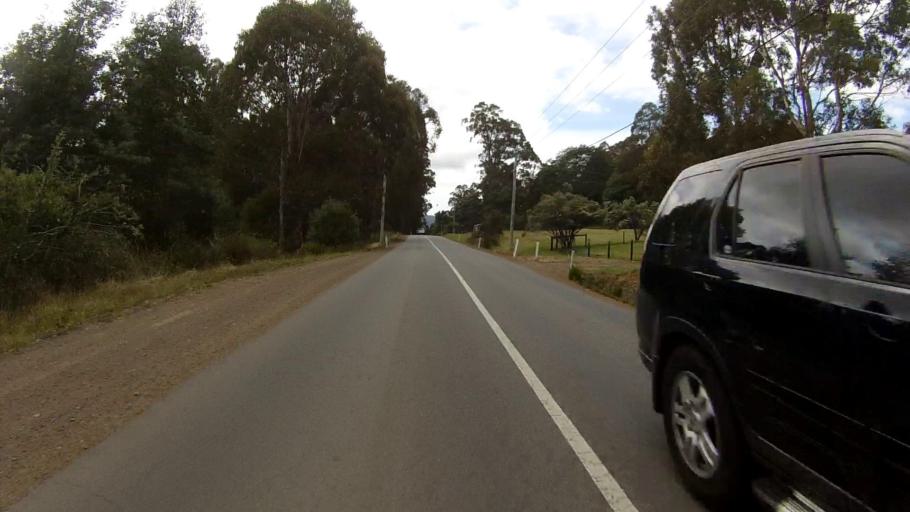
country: AU
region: Tasmania
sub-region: Kingborough
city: Kettering
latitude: -43.1177
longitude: 147.1875
